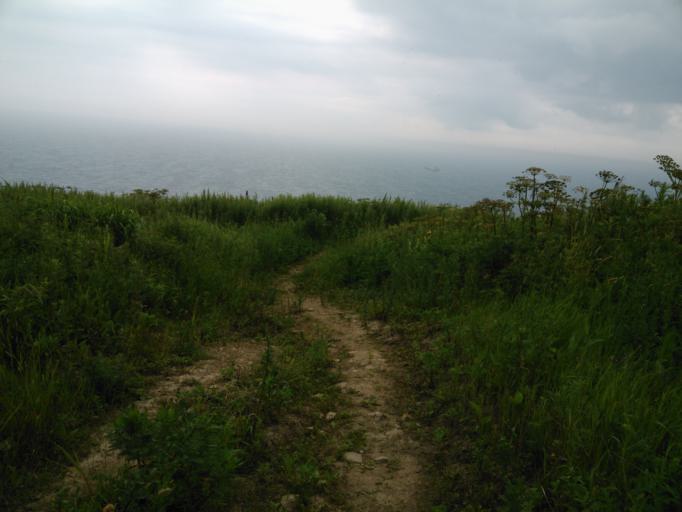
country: RU
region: Primorskiy
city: Vladivostok
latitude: 43.0946
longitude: 131.9882
